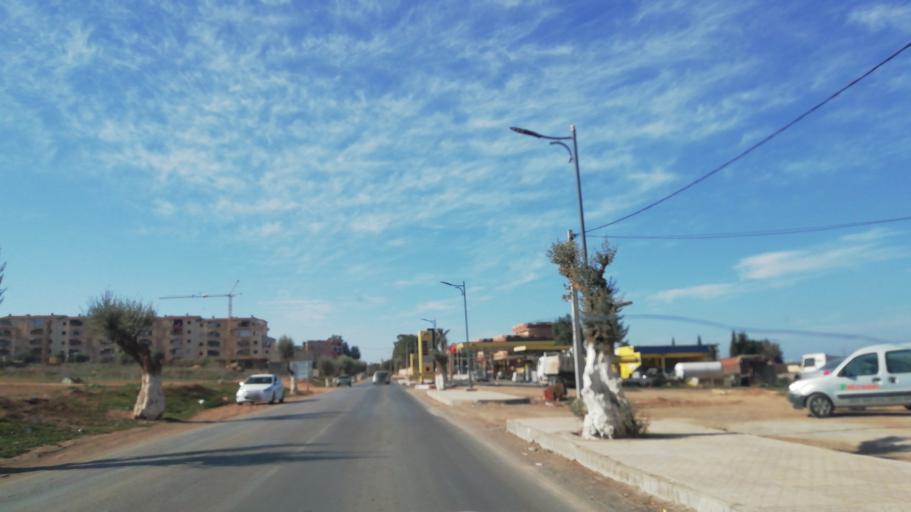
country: DZ
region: Tlemcen
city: Ouled Mimoun
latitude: 35.0275
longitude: -0.8819
